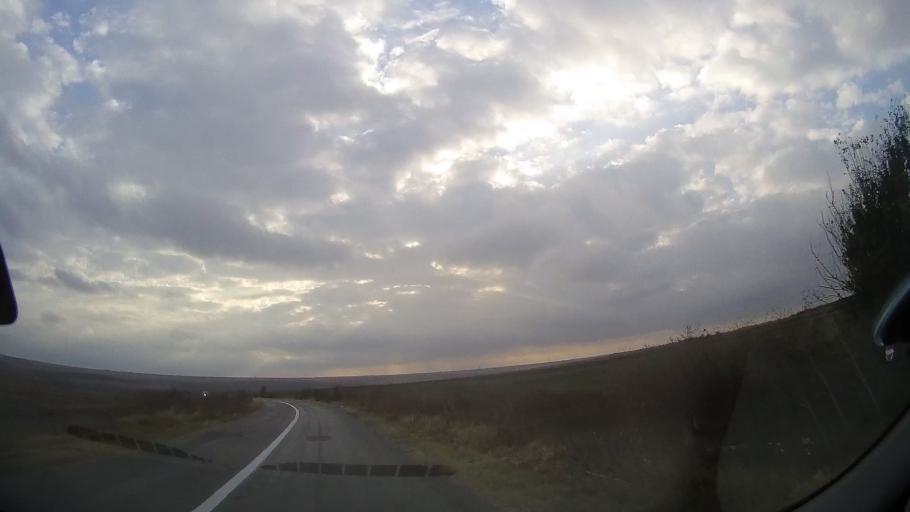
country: RO
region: Constanta
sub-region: Comuna Deleni
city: Pietreni
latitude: 44.1241
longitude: 28.1062
